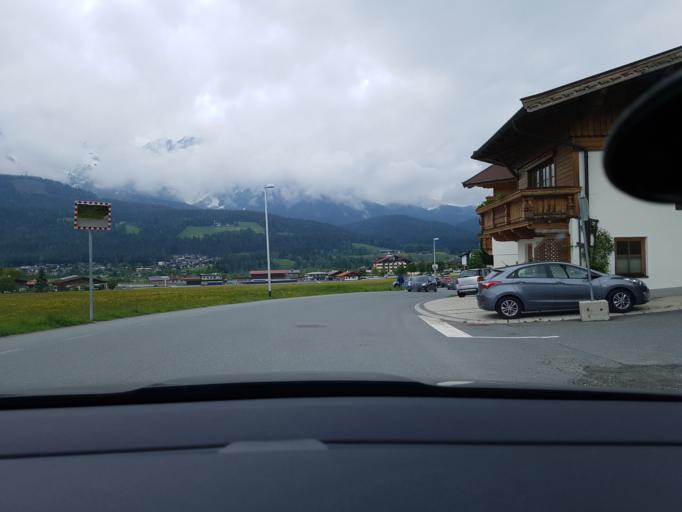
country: AT
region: Tyrol
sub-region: Politischer Bezirk Kufstein
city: Ellmau
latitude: 47.5117
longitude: 12.2957
